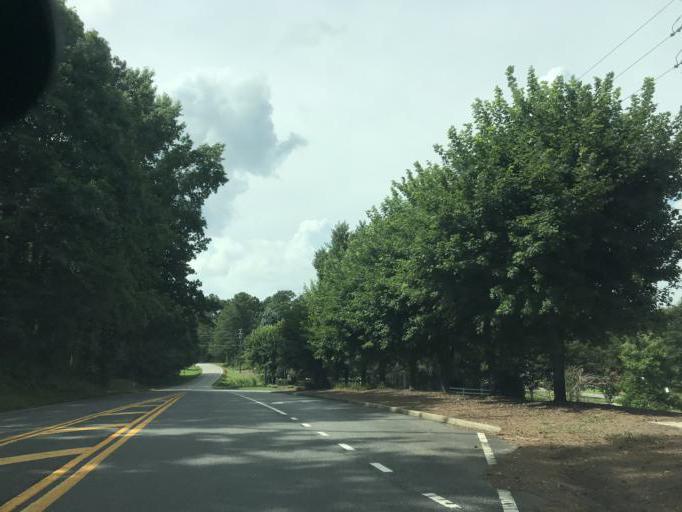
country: US
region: Georgia
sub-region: Forsyth County
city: Cumming
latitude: 34.2296
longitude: -84.2427
